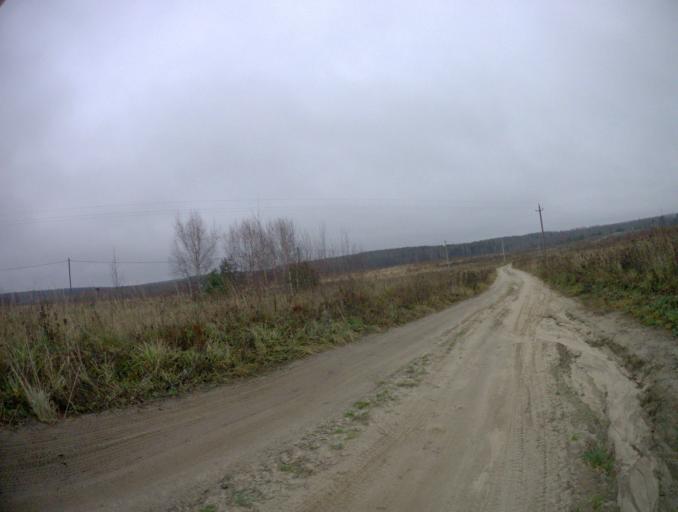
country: RU
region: Vladimir
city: Golovino
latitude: 55.9791
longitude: 40.4533
